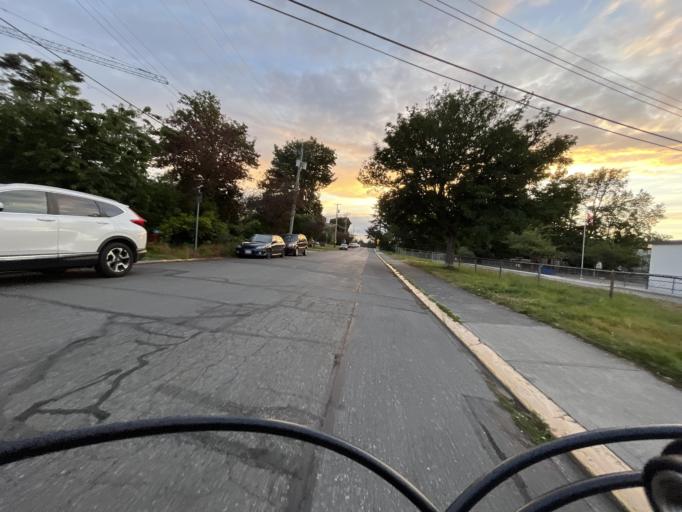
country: CA
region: British Columbia
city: Victoria
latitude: 48.4251
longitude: -123.4058
